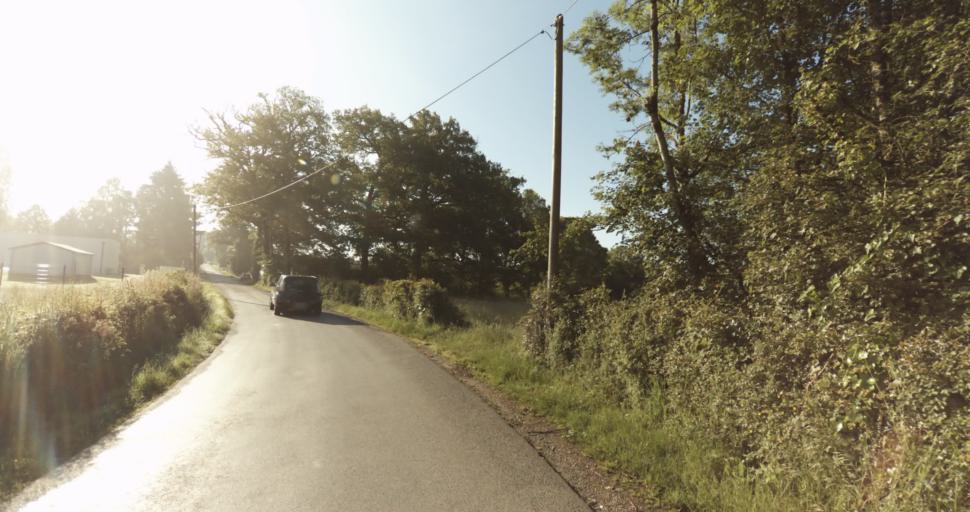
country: FR
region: Limousin
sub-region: Departement de la Haute-Vienne
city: Condat-sur-Vienne
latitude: 45.7821
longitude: 1.2850
